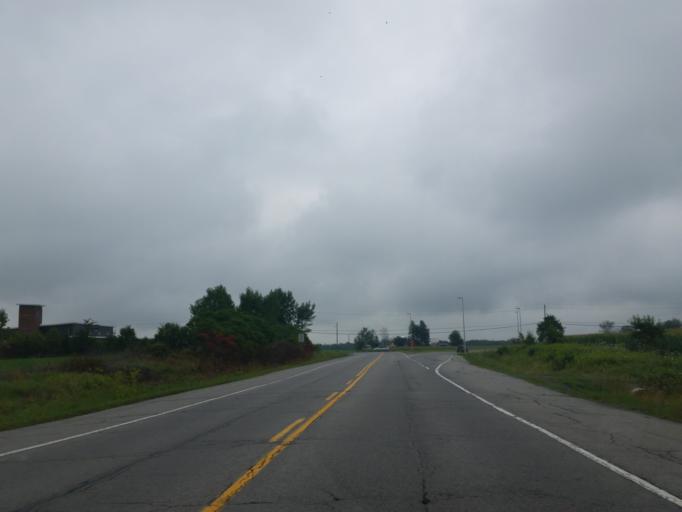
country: CA
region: Ontario
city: Clarence-Rockland
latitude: 45.3434
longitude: -75.3492
